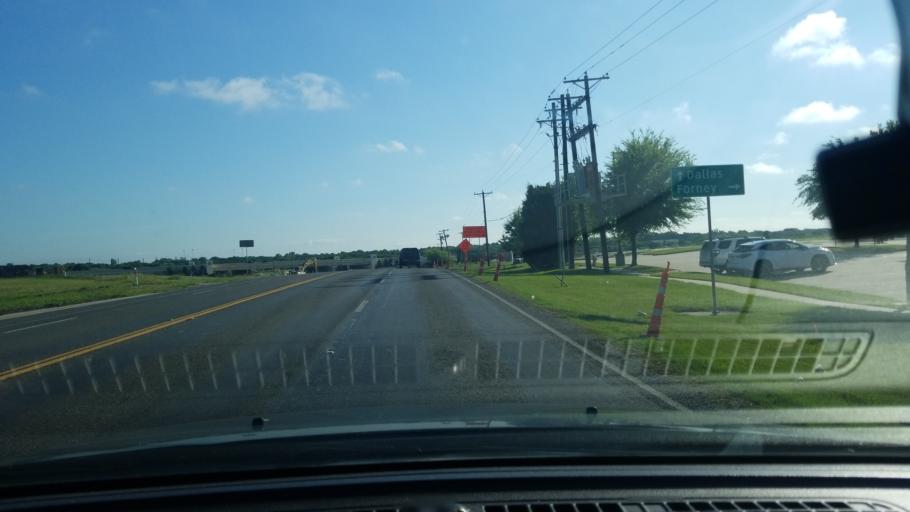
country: US
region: Texas
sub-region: Dallas County
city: Sunnyvale
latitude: 32.7817
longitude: -96.5645
